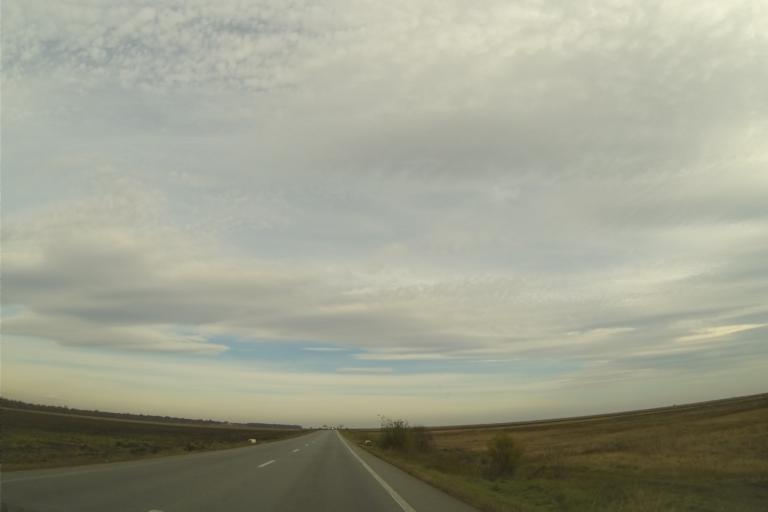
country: RO
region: Olt
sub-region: Comuna Priseaca
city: Priseaca
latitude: 44.4999
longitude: 24.4641
